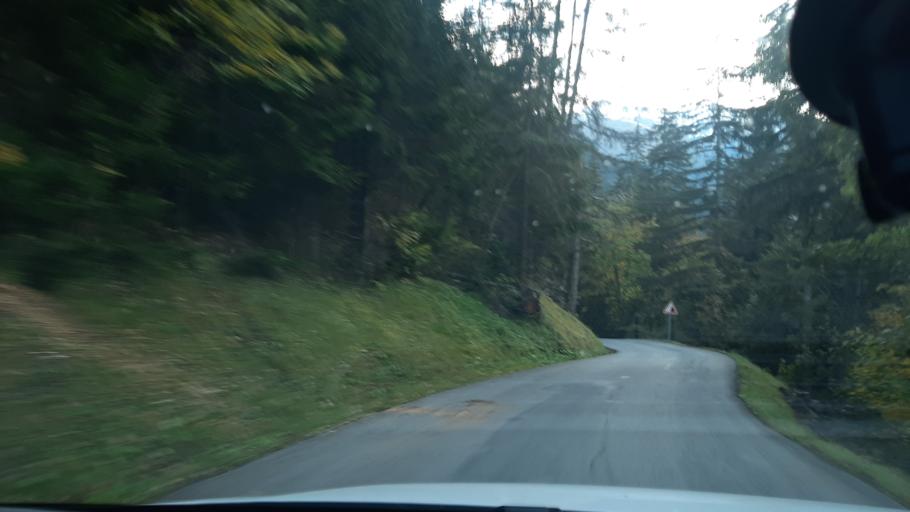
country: FR
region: Rhone-Alpes
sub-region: Departement de la Savoie
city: Saint-Jean-de-Maurienne
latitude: 45.2009
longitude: 6.3108
